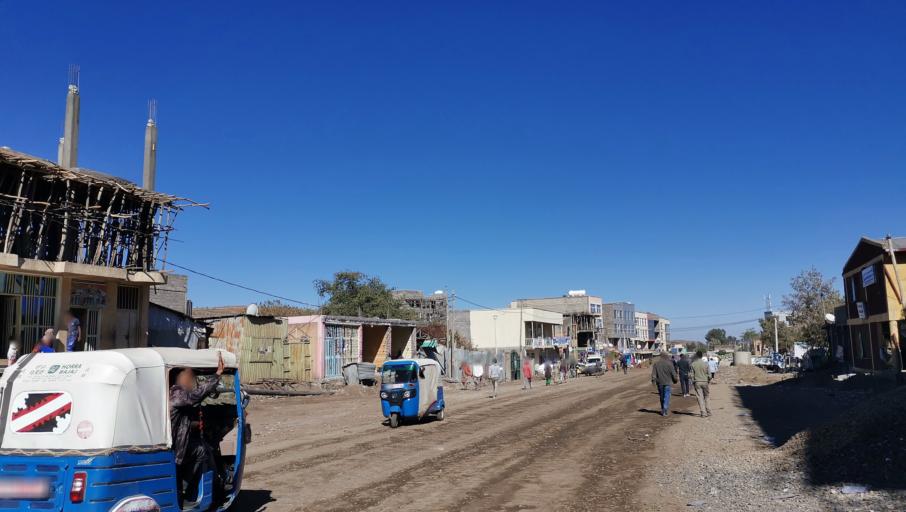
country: ET
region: Tigray
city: Korem
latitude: 12.6230
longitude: 39.0361
